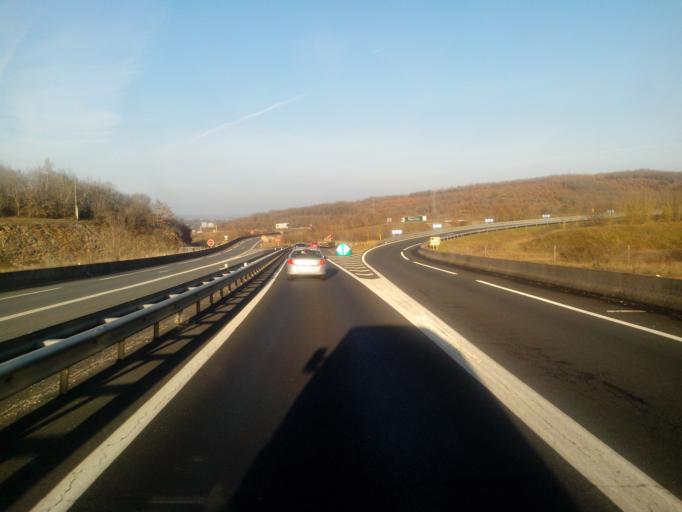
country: FR
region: Limousin
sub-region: Departement de la Correze
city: Brive-la-Gaillarde
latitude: 45.0619
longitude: 1.5034
